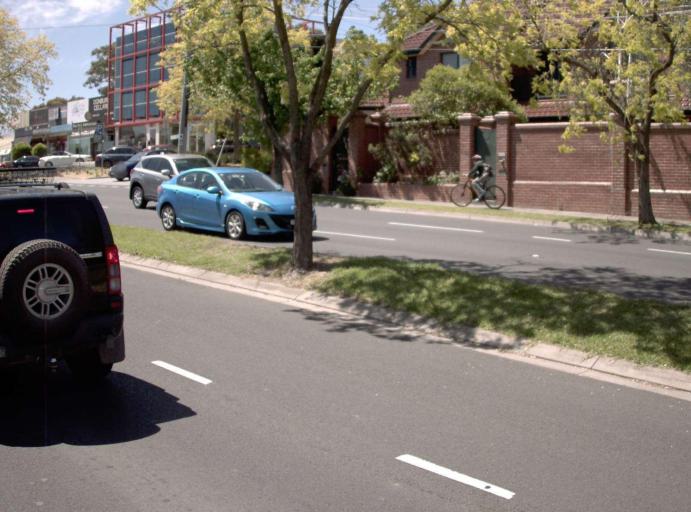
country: AU
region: Victoria
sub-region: Manningham
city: Donvale
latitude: -37.7832
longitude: 145.1630
